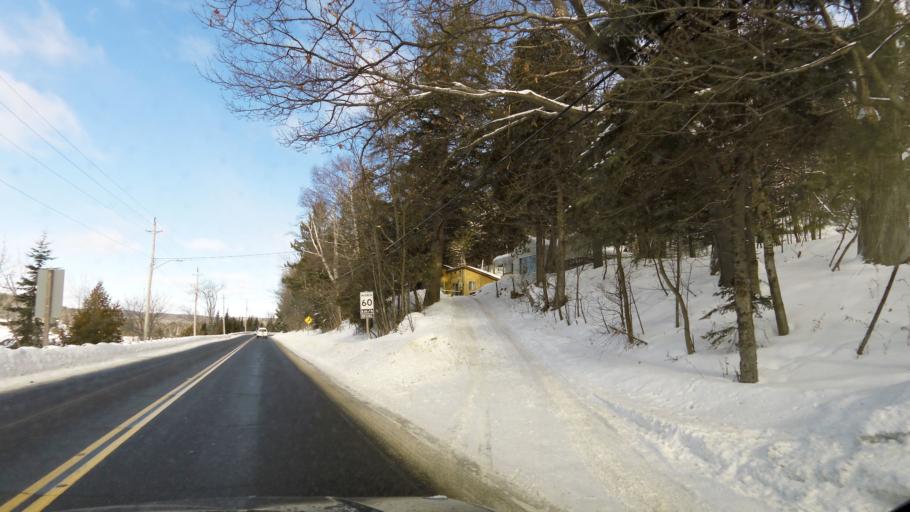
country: CA
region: Ontario
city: Bancroft
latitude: 45.0509
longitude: -78.5145
